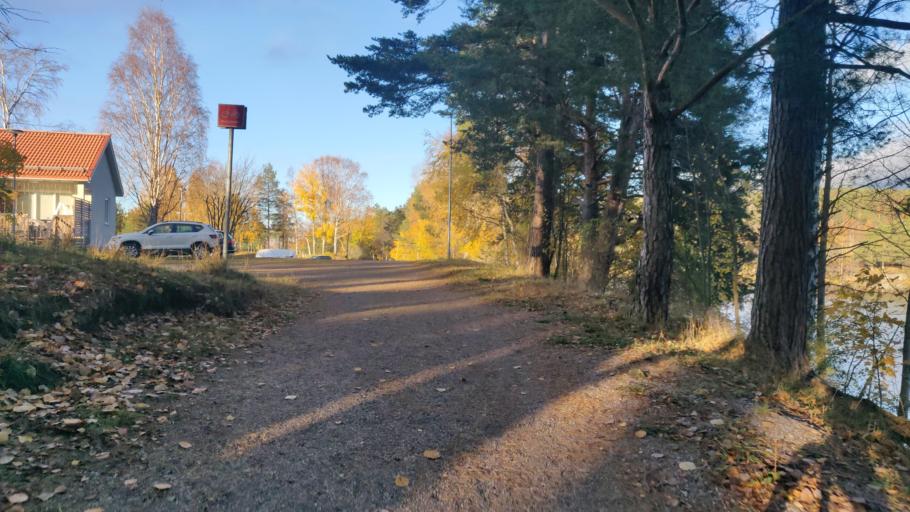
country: SE
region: Vaesternorrland
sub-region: Sundsvalls Kommun
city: Skottsund
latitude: 62.2962
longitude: 17.3832
